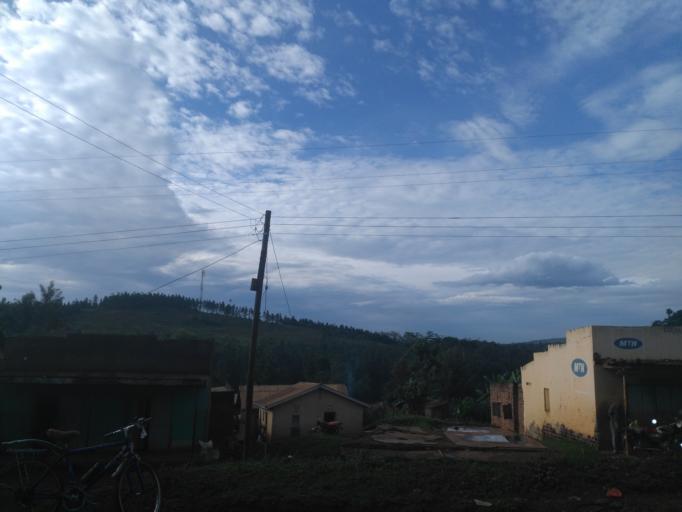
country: UG
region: Eastern Region
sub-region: Jinja District
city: Jinja
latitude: 0.4649
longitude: 33.1791
